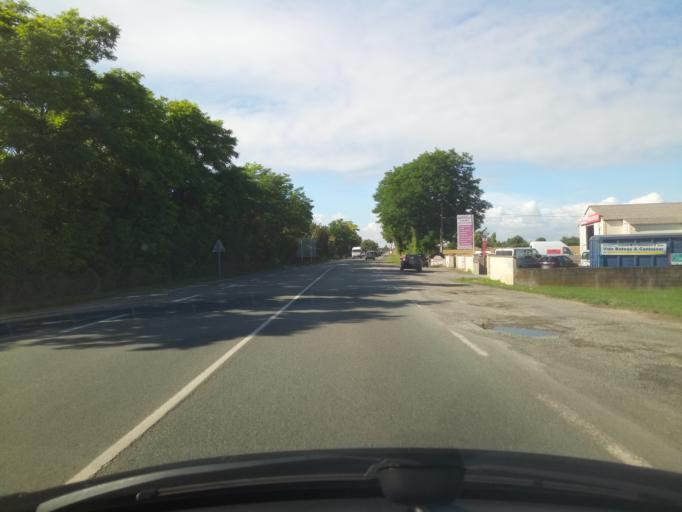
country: FR
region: Poitou-Charentes
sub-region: Departement de la Charente-Maritime
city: Marans
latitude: 46.2965
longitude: -0.9911
